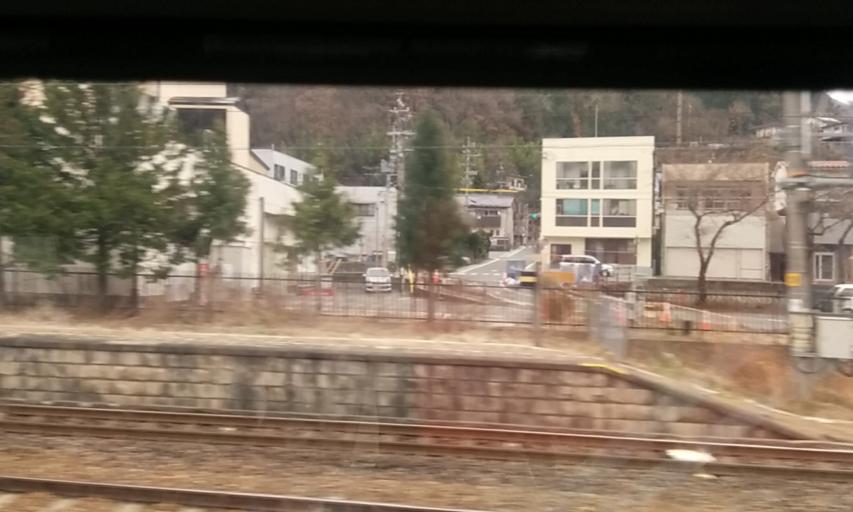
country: JP
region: Nagano
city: Ina
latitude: 35.7830
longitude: 137.6925
